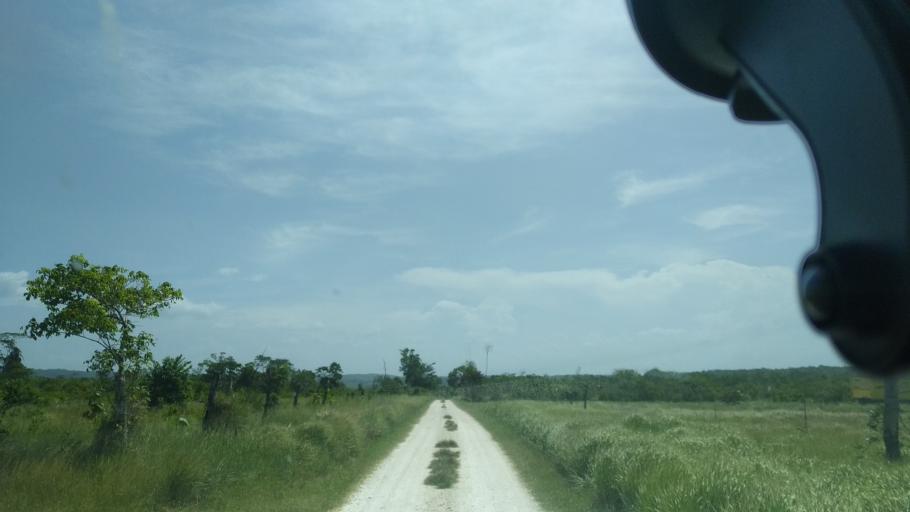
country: BZ
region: Cayo
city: San Ignacio
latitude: 17.2871
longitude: -89.0804
